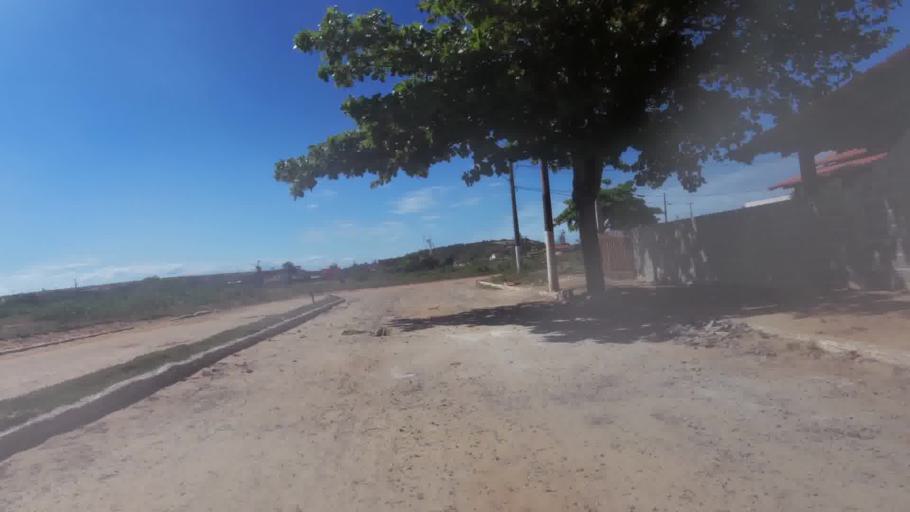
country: BR
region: Espirito Santo
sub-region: Marataizes
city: Marataizes
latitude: -21.1929
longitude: -40.9319
